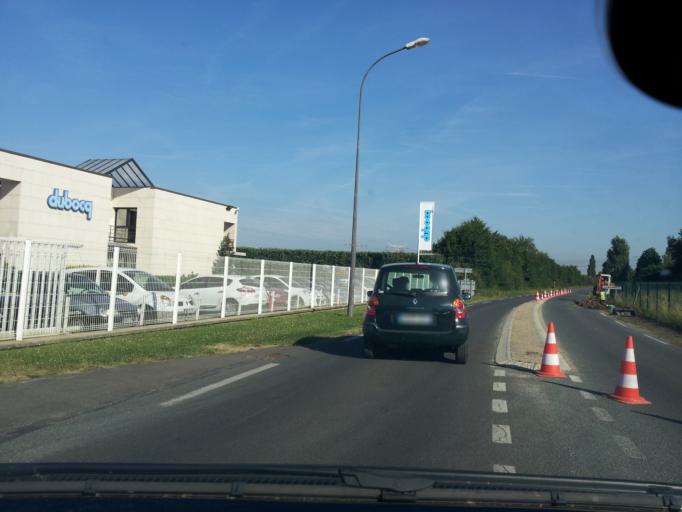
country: FR
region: Ile-de-France
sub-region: Departement de l'Essonne
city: Saint-Vrain
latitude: 48.5458
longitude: 2.3208
